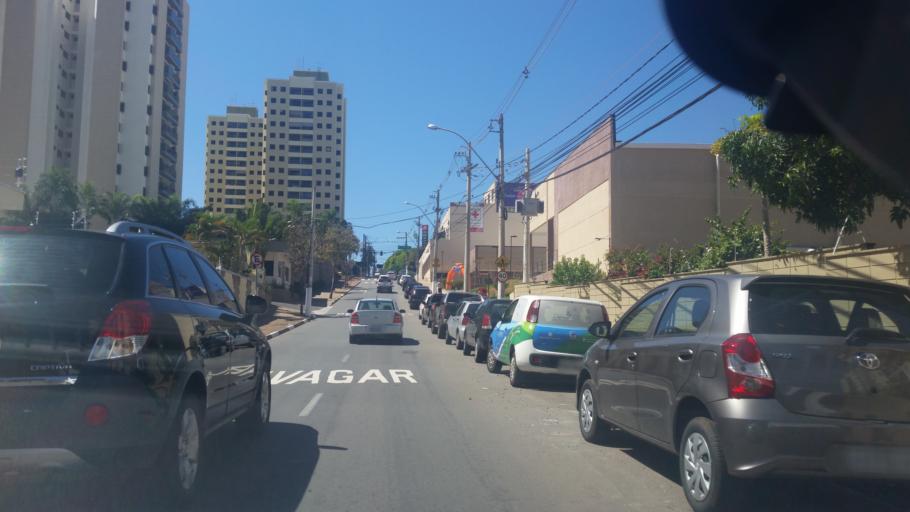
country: BR
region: Sao Paulo
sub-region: Campinas
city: Campinas
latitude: -22.8557
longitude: -47.0475
